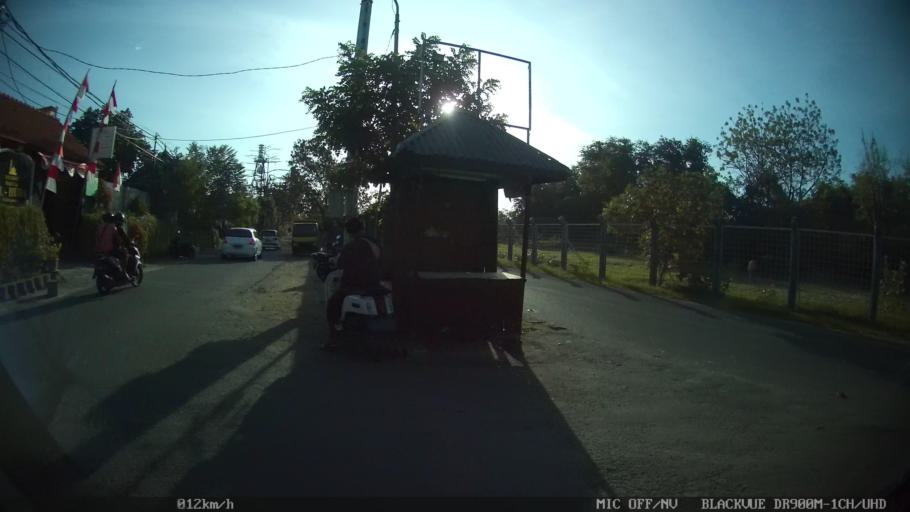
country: ID
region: Bali
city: Kelanabian
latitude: -8.7562
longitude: 115.1697
